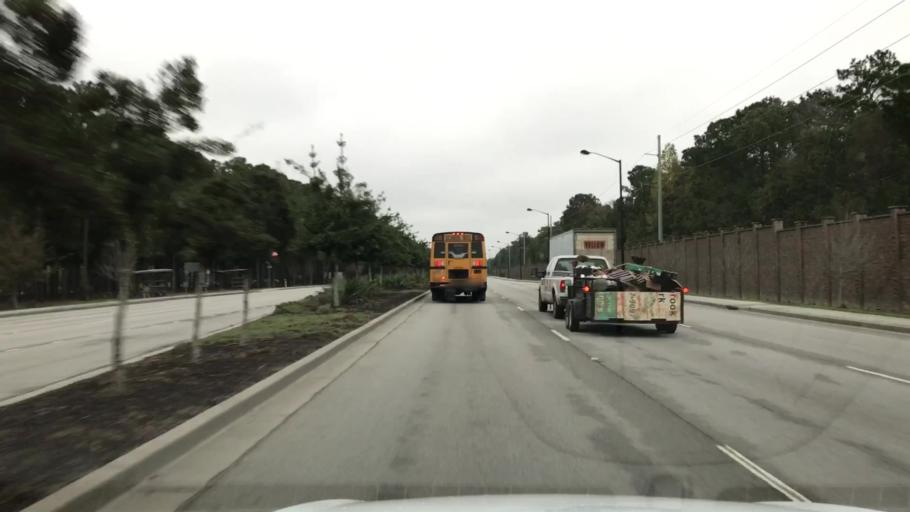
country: US
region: South Carolina
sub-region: Charleston County
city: Isle of Palms
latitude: 32.8758
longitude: -79.7700
